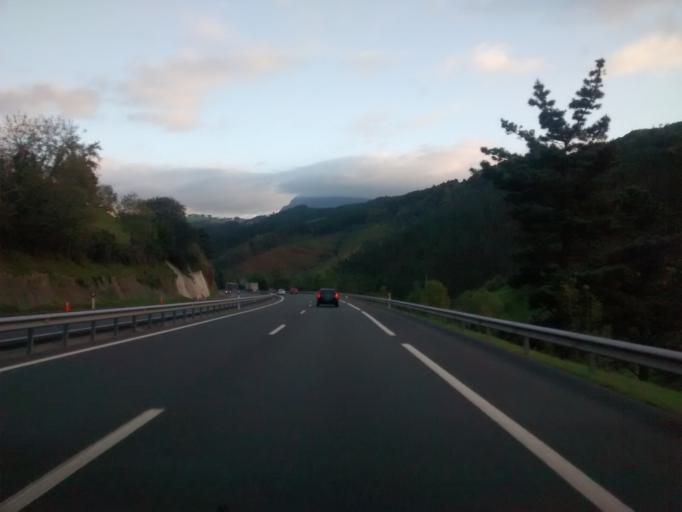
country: ES
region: Basque Country
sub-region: Provincia de Guipuzcoa
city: Deba
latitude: 43.2746
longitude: -2.3098
